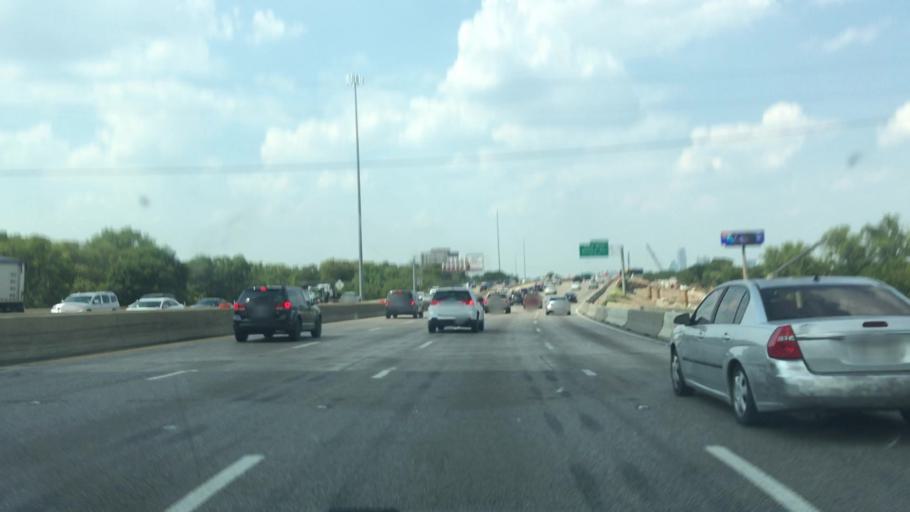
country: US
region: Texas
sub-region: Dallas County
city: Dallas
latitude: 32.7303
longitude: -96.8252
